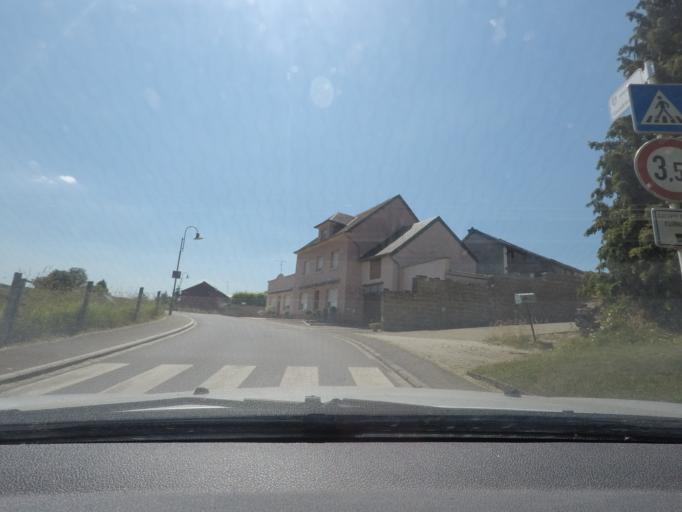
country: LU
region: Diekirch
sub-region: Canton de Redange
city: Ell
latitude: 49.7576
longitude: 5.8253
